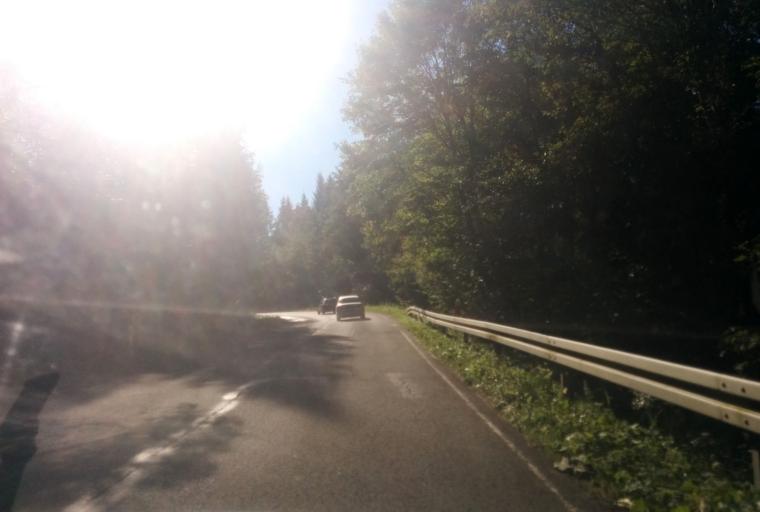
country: PL
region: Subcarpathian Voivodeship
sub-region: Powiat leski
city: Cisna
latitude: 49.1934
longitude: 22.3731
